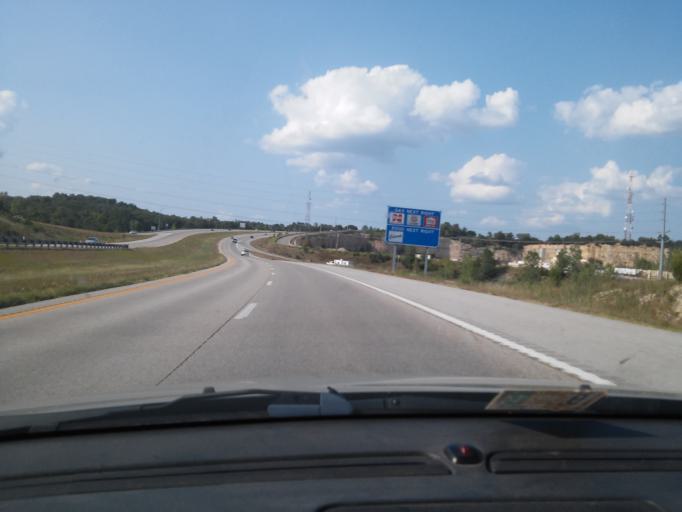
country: US
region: Missouri
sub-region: Cole County
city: Jefferson City
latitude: 38.5405
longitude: -92.2086
